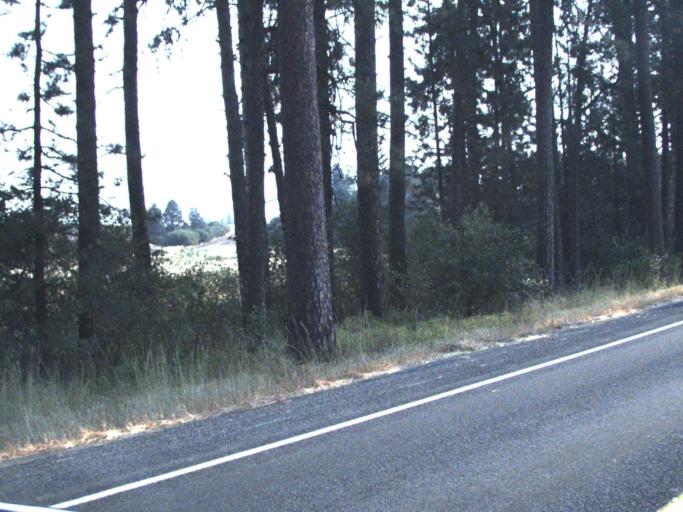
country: US
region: Idaho
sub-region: Benewah County
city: Plummer
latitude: 47.4421
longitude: -117.0653
